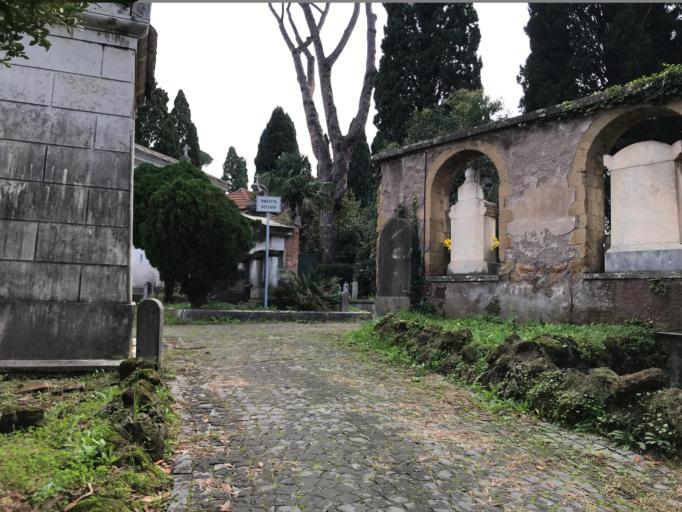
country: IT
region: Latium
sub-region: Citta metropolitana di Roma Capitale
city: Rome
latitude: 41.9036
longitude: 12.5210
